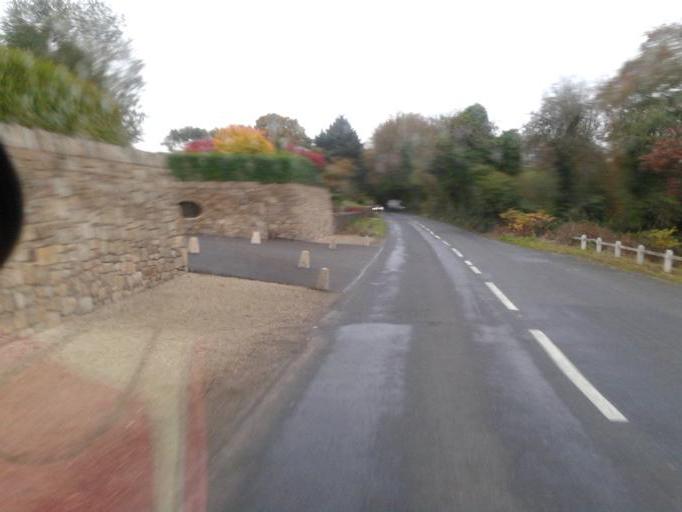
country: IE
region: Munster
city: Ballina
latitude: 52.7976
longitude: -8.4345
